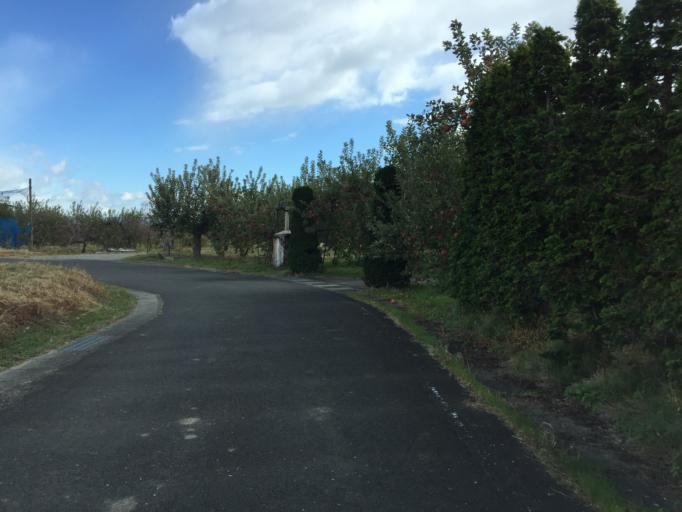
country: JP
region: Fukushima
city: Fukushima-shi
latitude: 37.8091
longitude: 140.4339
